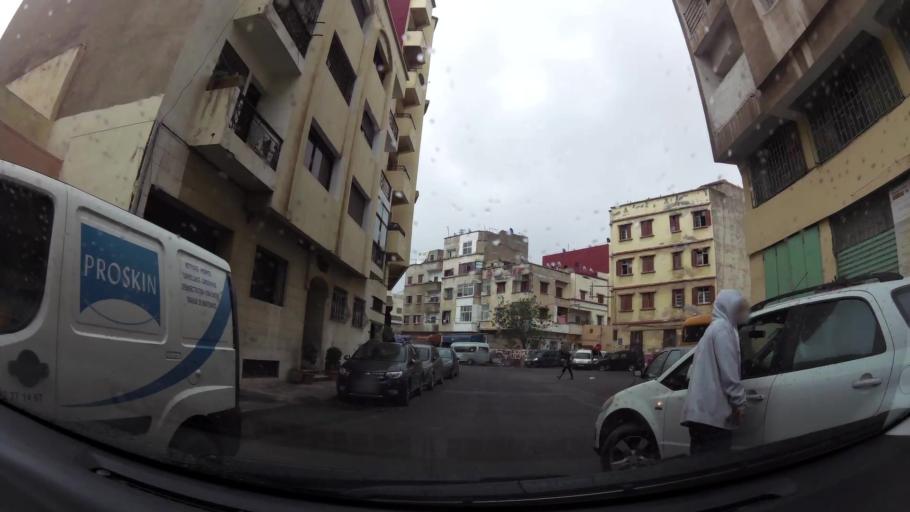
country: MA
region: Grand Casablanca
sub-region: Casablanca
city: Casablanca
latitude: 33.6016
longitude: -7.6445
